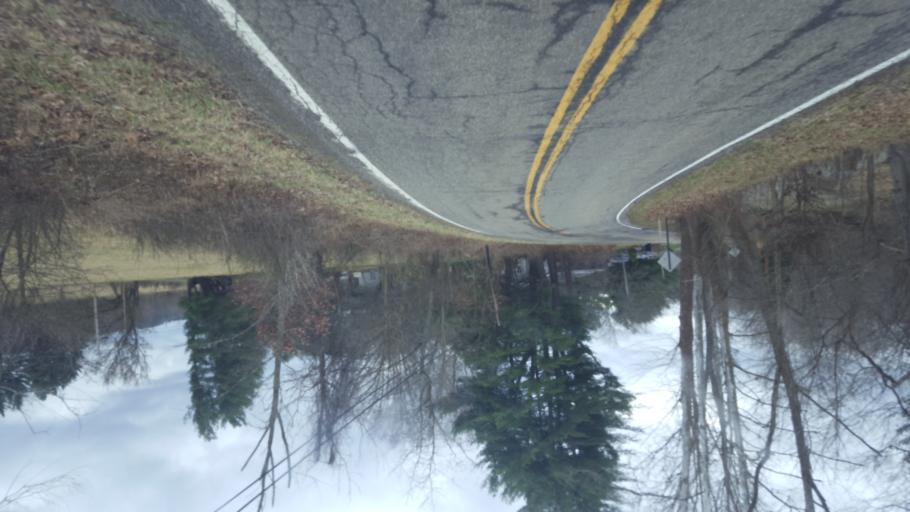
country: US
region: Ohio
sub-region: Licking County
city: Newark
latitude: 40.1684
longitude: -82.2965
